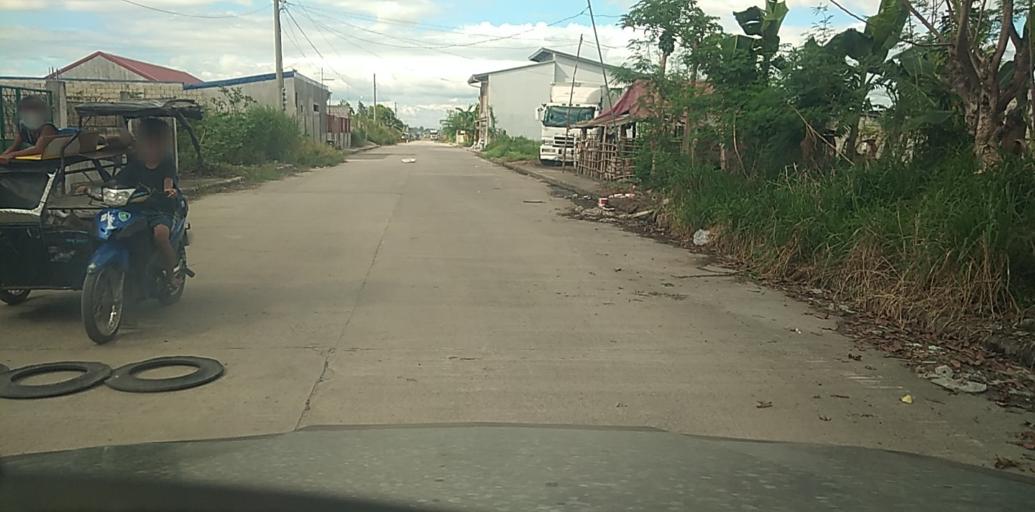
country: PH
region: Central Luzon
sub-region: Province of Pampanga
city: Buensuseso
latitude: 15.1801
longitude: 120.6670
